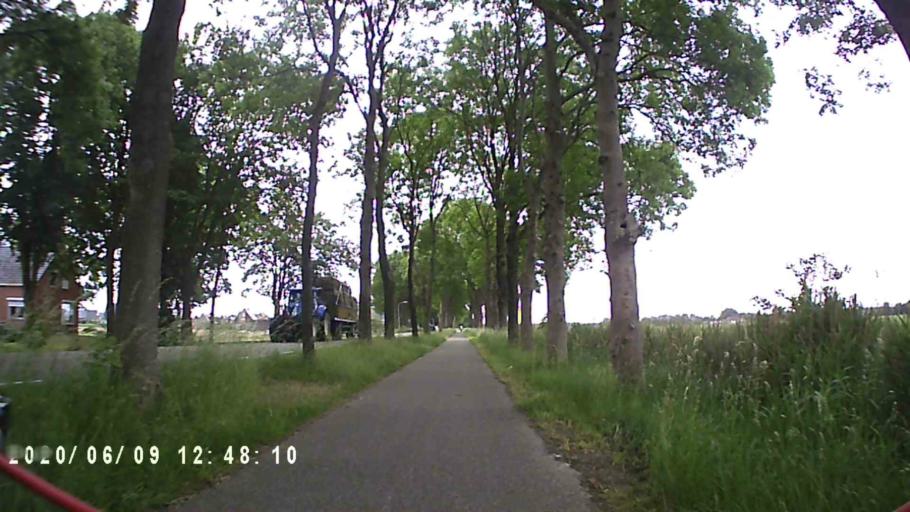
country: NL
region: Groningen
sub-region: Gemeente Groningen
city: Oosterpark
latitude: 53.2248
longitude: 6.6447
